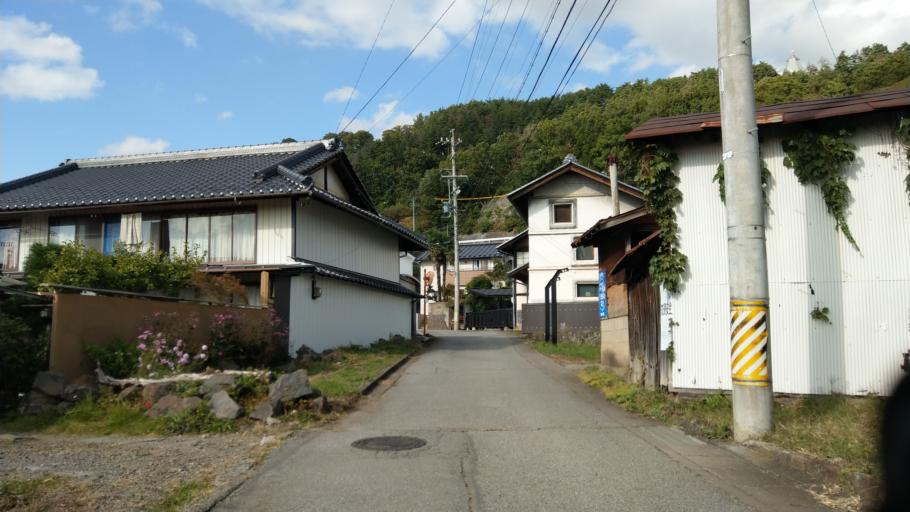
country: JP
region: Nagano
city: Komoro
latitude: 36.3405
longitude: 138.4179
